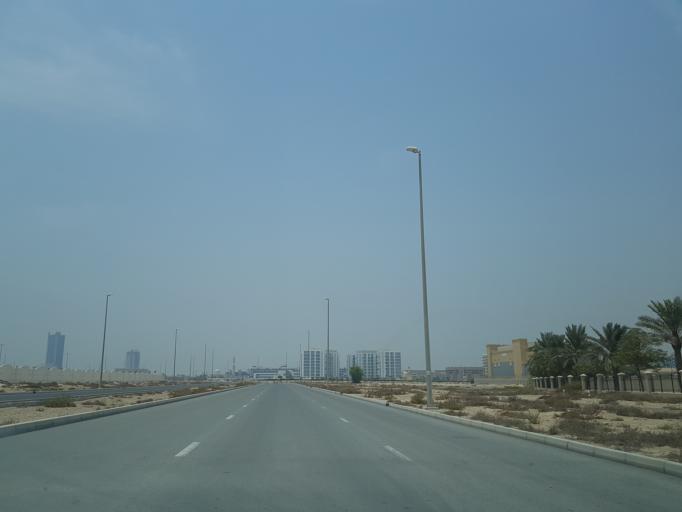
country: AE
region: Dubai
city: Dubai
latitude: 25.0351
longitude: 55.2479
